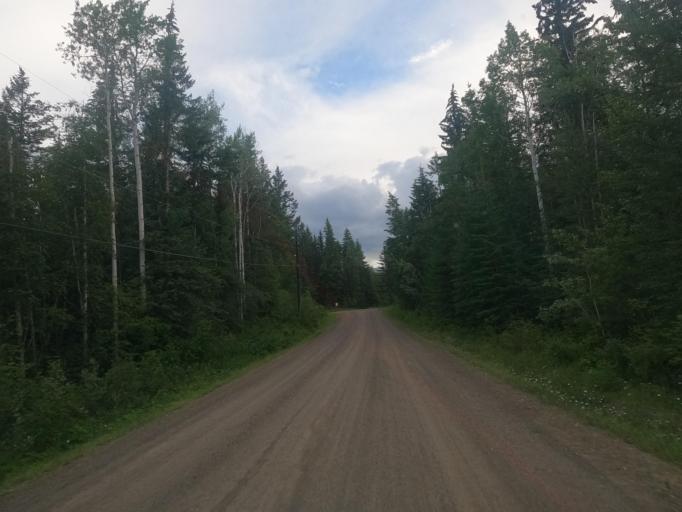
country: CA
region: British Columbia
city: Golden
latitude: 51.4532
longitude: -117.0037
